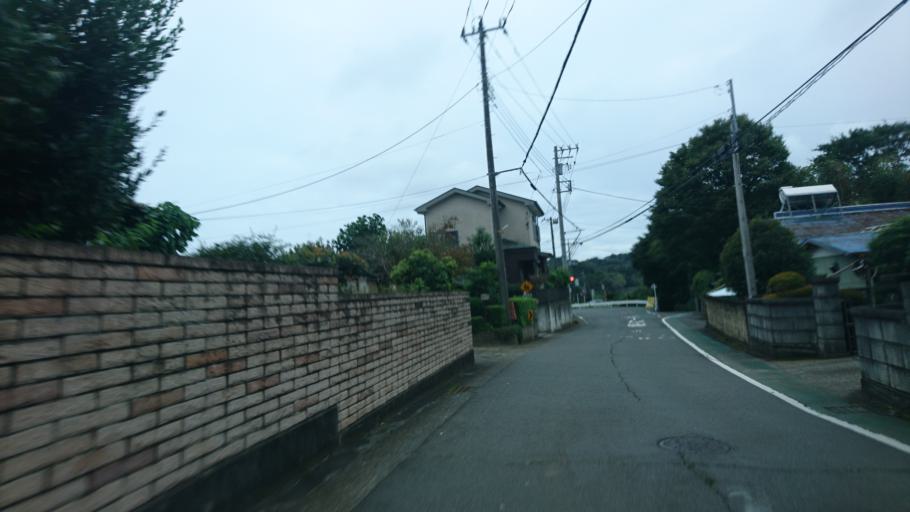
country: JP
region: Kanagawa
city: Atsugi
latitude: 35.4867
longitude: 139.3238
